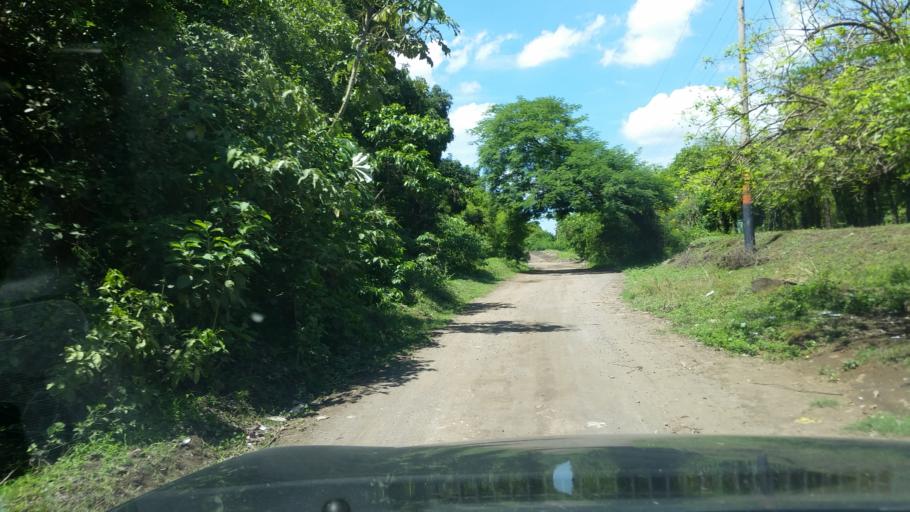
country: NI
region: Chinandega
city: Puerto Morazan
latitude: 12.7624
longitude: -87.1333
